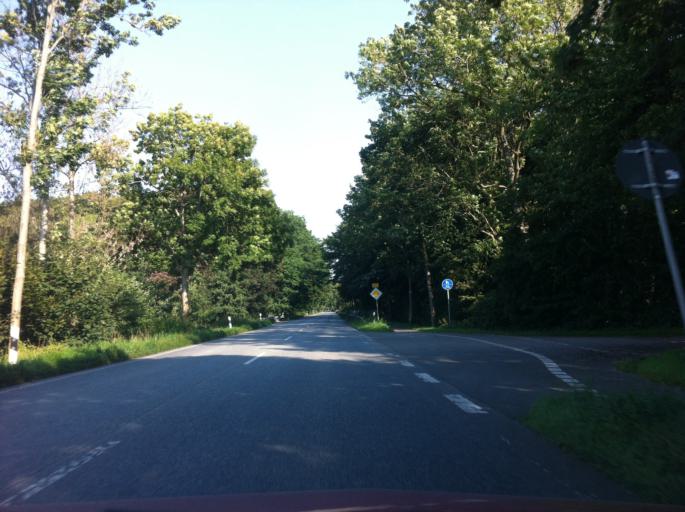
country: DE
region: Schleswig-Holstein
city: Wangels
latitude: 54.3008
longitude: 10.7558
